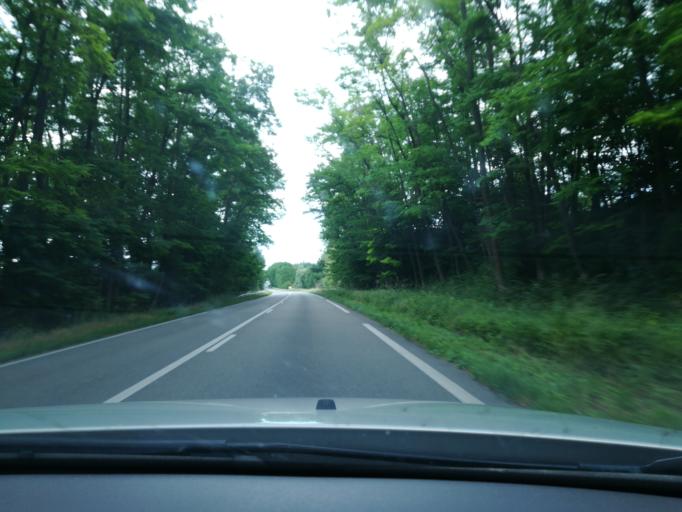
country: FR
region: Alsace
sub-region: Departement du Bas-Rhin
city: Steinbourg
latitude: 48.7687
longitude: 7.4034
